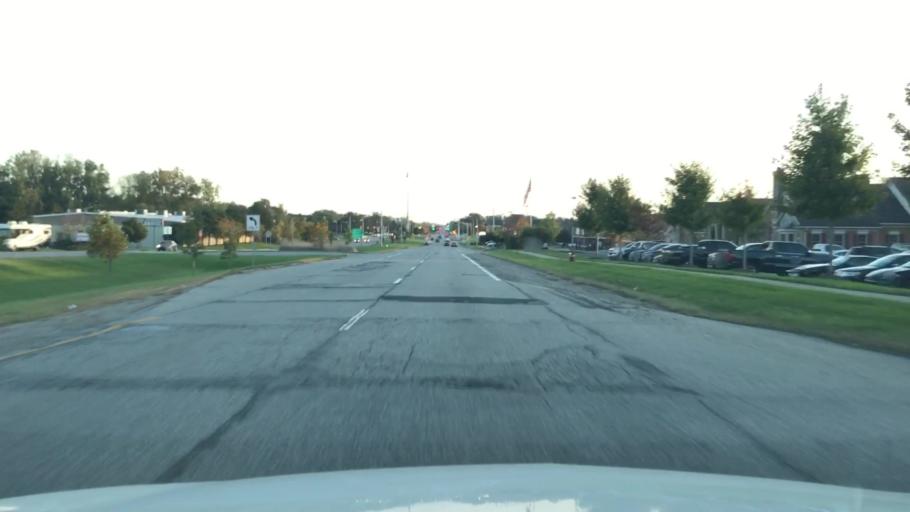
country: US
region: Michigan
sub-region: Macomb County
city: Utica
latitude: 42.6289
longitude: -83.0525
